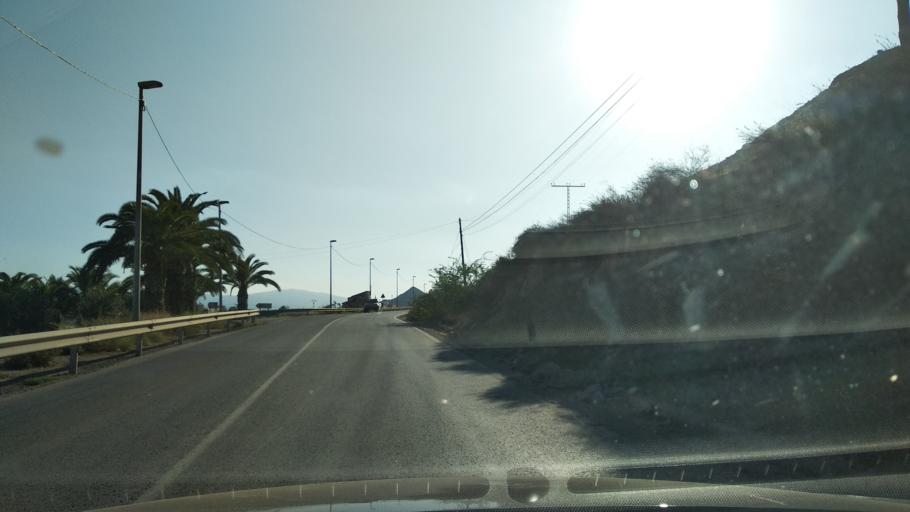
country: ES
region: Murcia
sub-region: Murcia
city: Santomera
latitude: 38.0542
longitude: -1.0532
